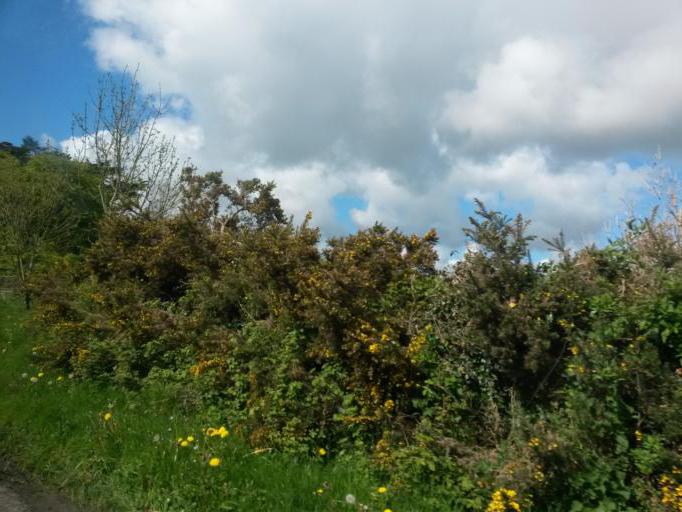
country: IE
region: Leinster
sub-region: Loch Garman
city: Loch Garman
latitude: 52.3621
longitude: -6.5101
